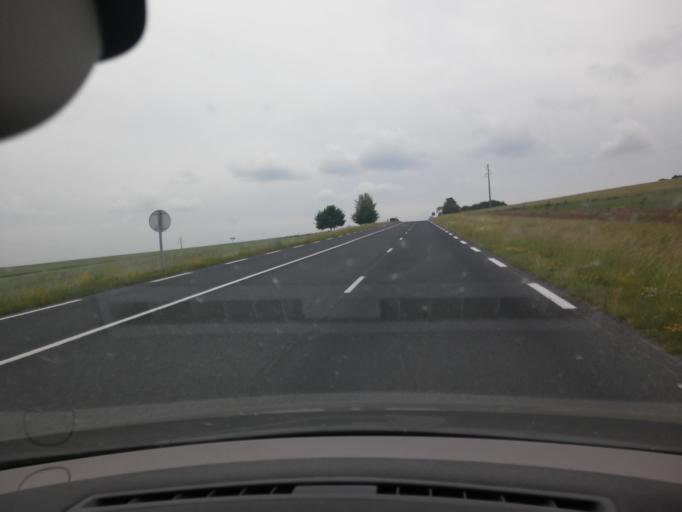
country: FR
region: Lorraine
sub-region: Departement de la Meuse
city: Saint-Mihiel
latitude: 48.8737
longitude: 5.5219
